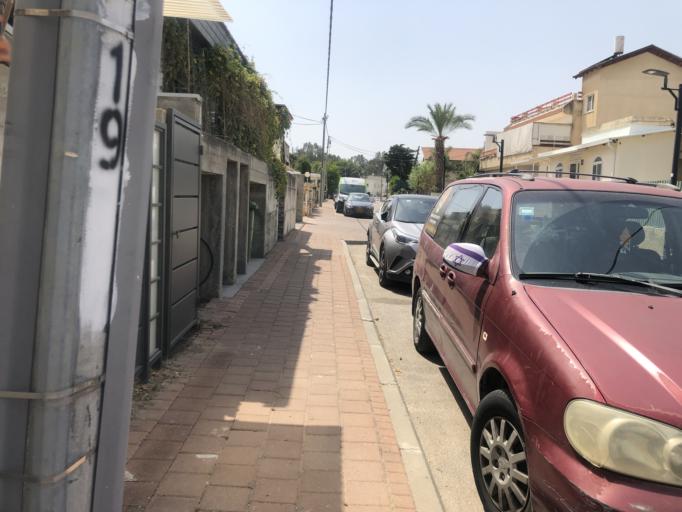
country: IL
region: Central District
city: Rosh Ha'Ayin
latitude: 32.0950
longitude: 34.9412
